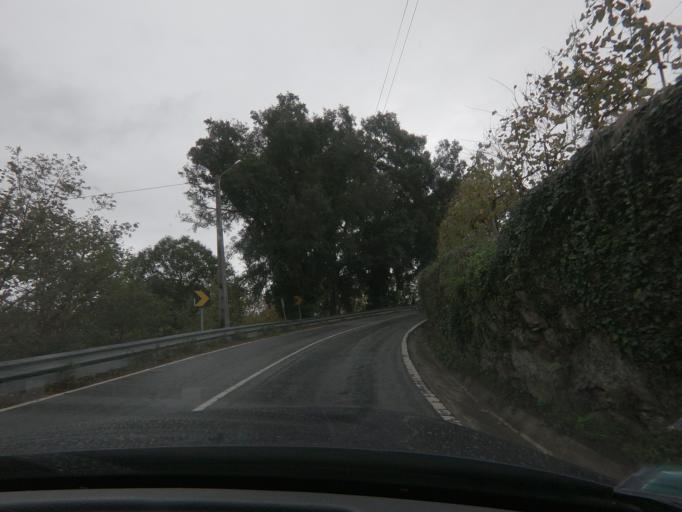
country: PT
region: Braga
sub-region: Celorico de Basto
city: Celorico de Basto
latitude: 41.4159
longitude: -7.9901
